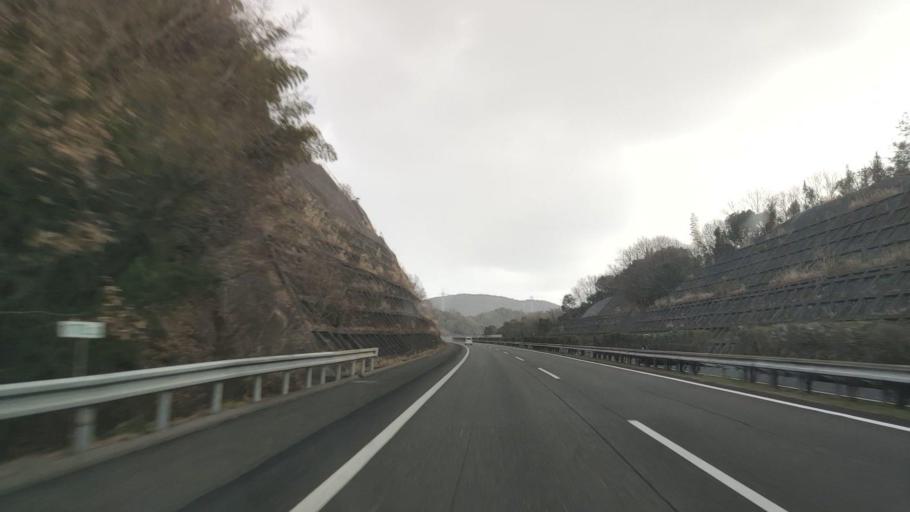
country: JP
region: Okayama
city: Kasaoka
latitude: 34.5321
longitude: 133.5307
